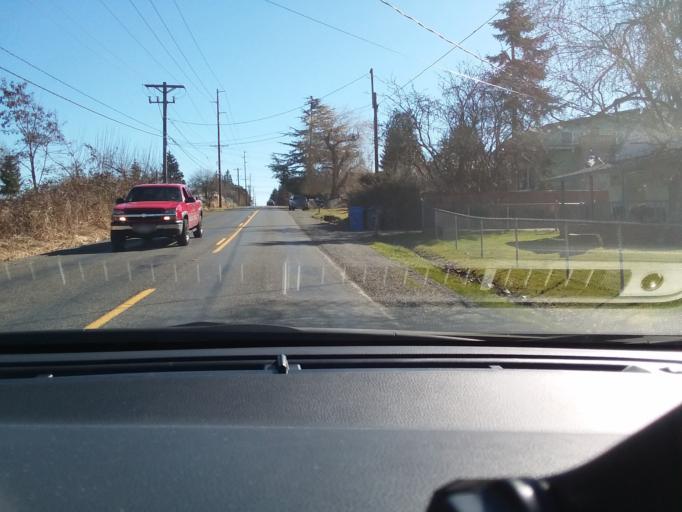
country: US
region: Washington
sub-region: Pierce County
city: Midland
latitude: 47.1699
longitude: -122.3916
